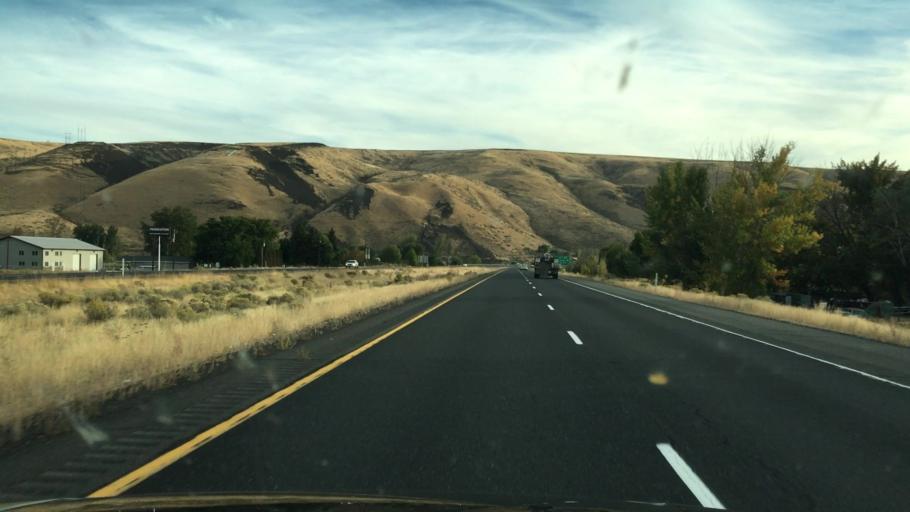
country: US
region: Washington
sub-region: Yakima County
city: Selah
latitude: 46.6573
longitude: -120.4970
